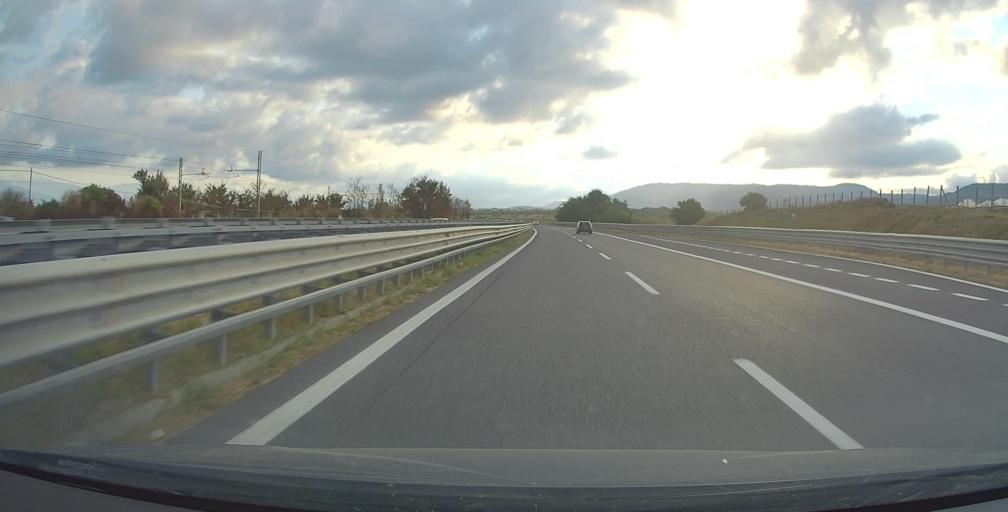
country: IT
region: Calabria
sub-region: Provincia di Catanzaro
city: Acconia
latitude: 38.8230
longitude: 16.2466
